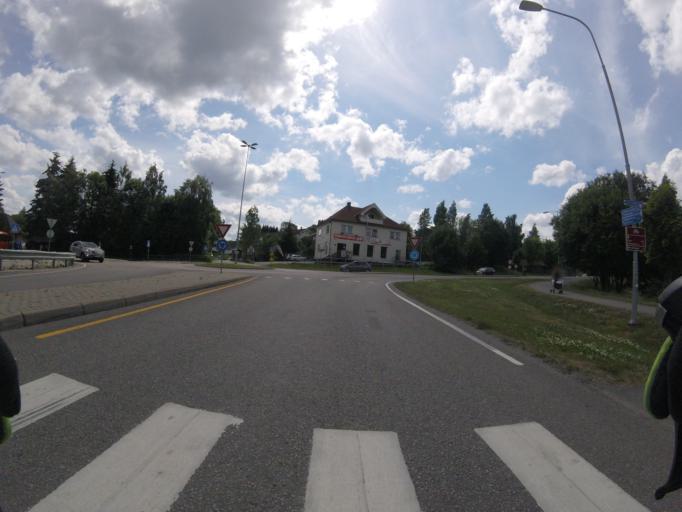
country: NO
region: Akershus
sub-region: Skedsmo
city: Lillestrom
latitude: 59.9574
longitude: 11.0159
